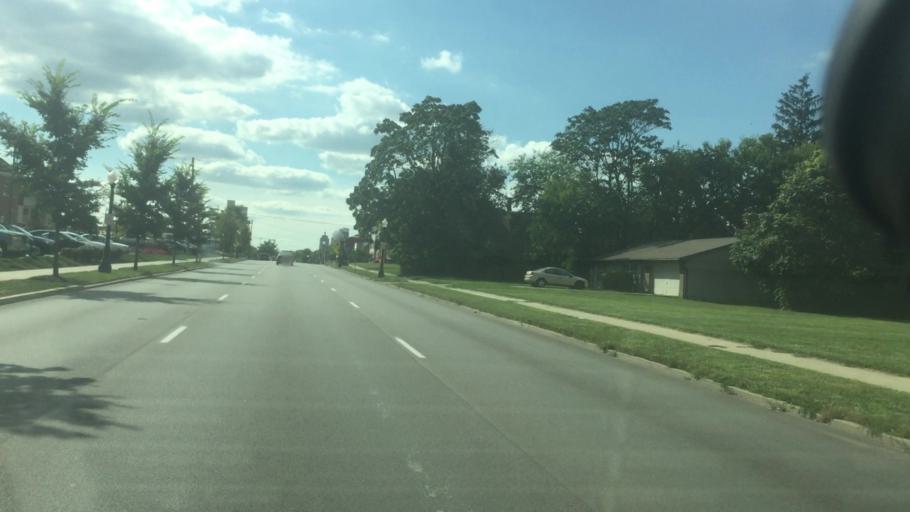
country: US
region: Indiana
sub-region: Allen County
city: Fort Wayne
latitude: 41.0791
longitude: -85.1159
